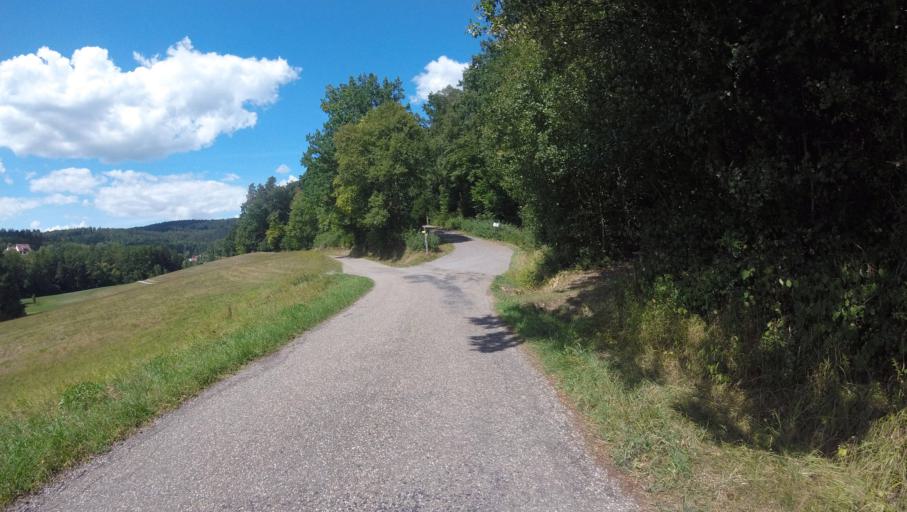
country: DE
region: Baden-Wuerttemberg
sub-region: Regierungsbezirk Stuttgart
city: Oppenweiler
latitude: 48.9950
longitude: 9.4474
